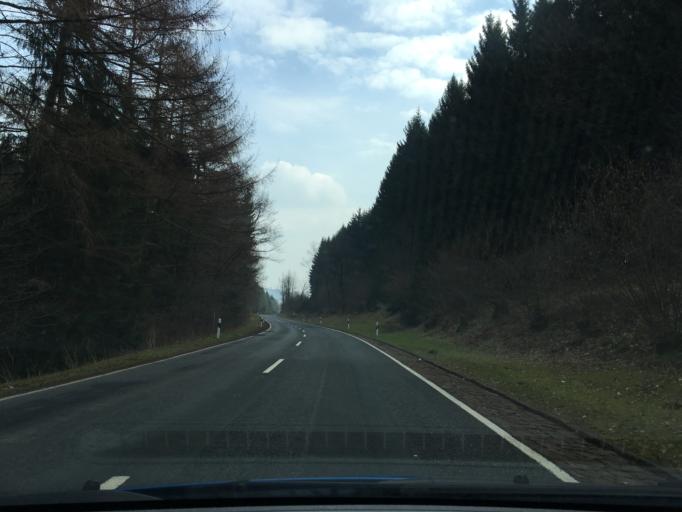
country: DE
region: Lower Saxony
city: Dassel
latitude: 51.7992
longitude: 9.6607
